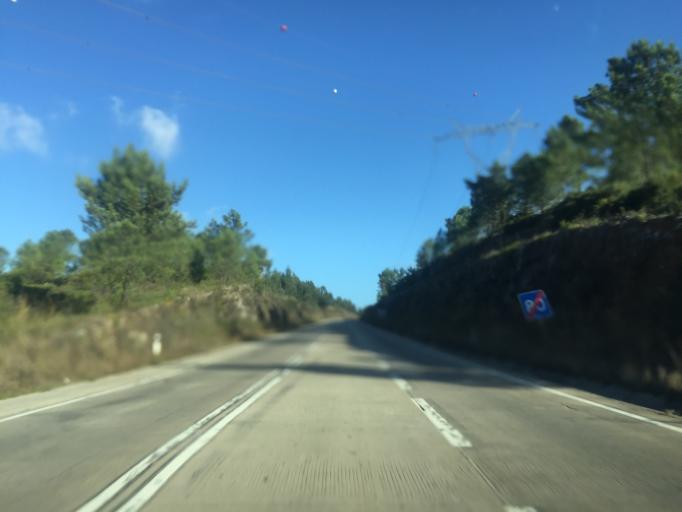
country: PT
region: Santarem
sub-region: Rio Maior
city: Rio Maior
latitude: 39.3480
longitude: -8.9715
